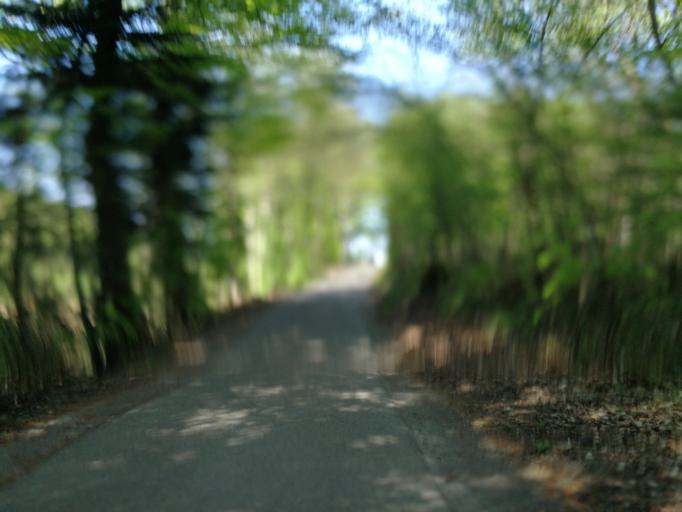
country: CH
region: Zurich
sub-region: Bezirk Hinwil
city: Hinwil
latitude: 47.3008
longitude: 8.8196
